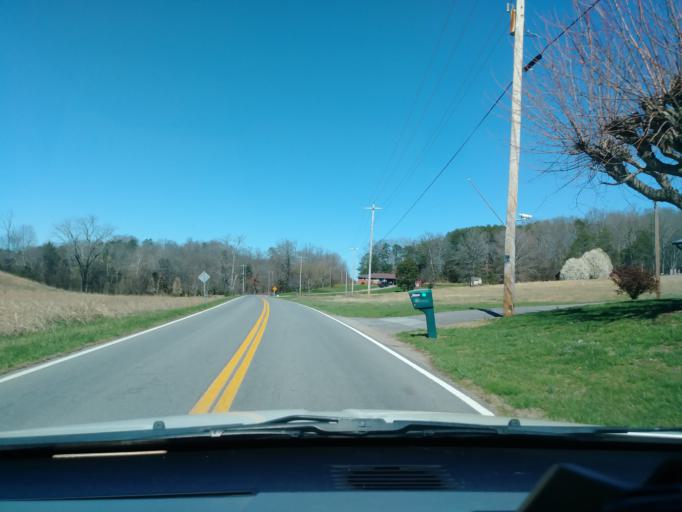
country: US
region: Tennessee
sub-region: Cocke County
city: Newport
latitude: 35.9762
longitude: -83.0596
